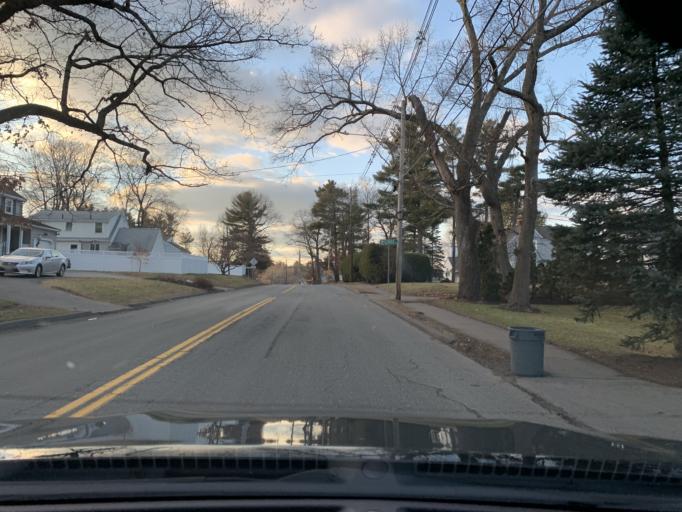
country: US
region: Massachusetts
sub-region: Essex County
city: Lynnfield
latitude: 42.5273
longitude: -71.0286
